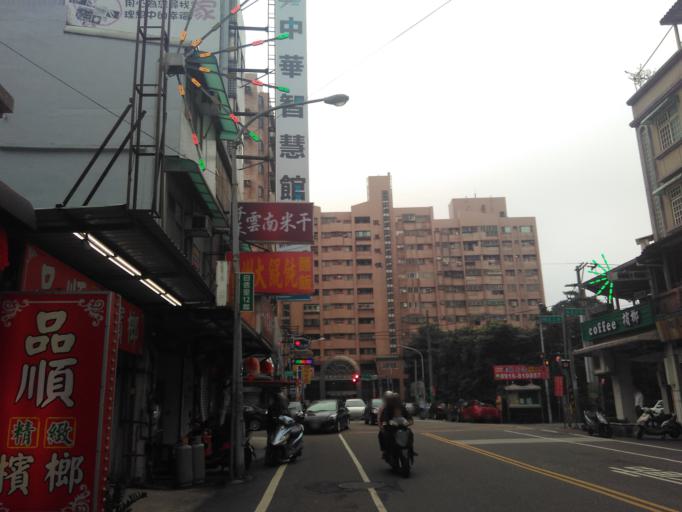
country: TW
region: Taiwan
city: Taoyuan City
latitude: 24.9637
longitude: 121.2541
